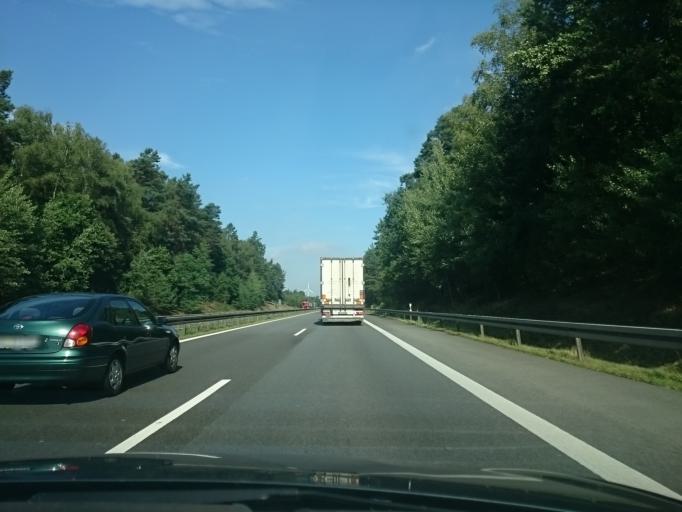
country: DE
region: Brandenburg
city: Bronkow
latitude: 51.7012
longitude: 13.8996
